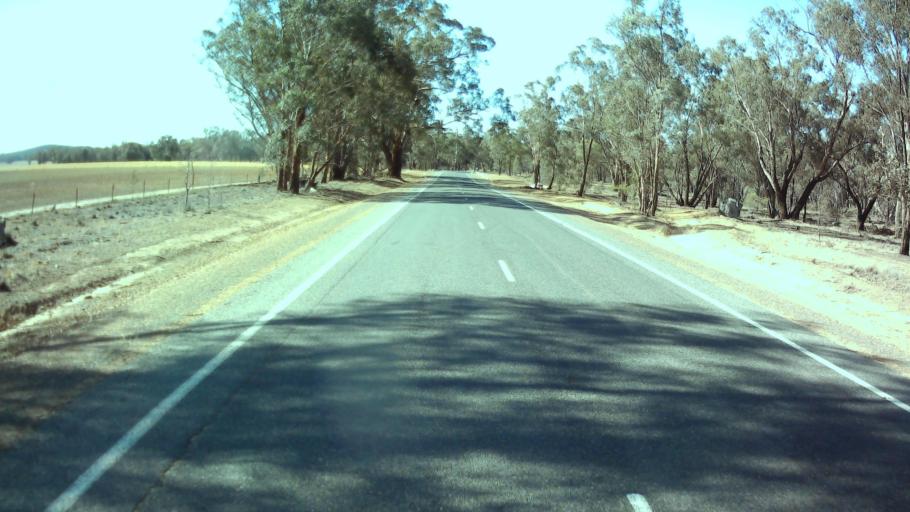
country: AU
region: New South Wales
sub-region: Weddin
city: Grenfell
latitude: -33.7665
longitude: 148.0826
